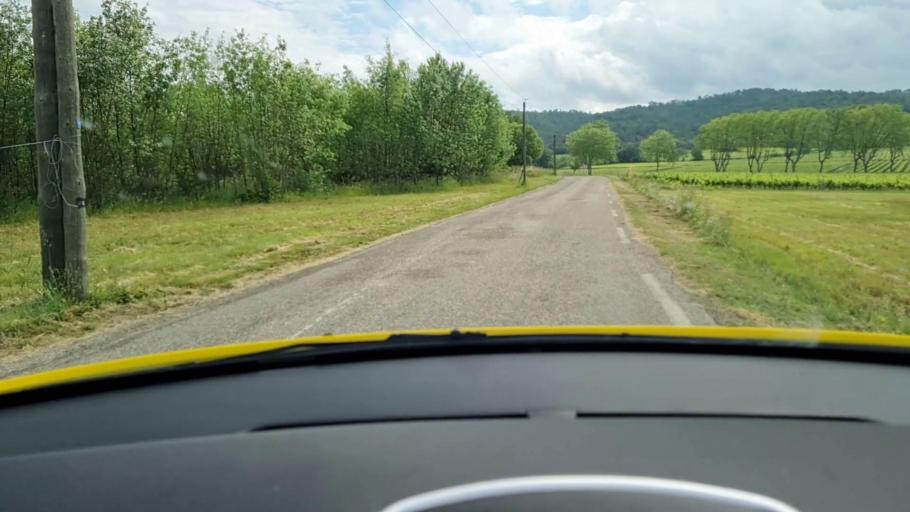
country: FR
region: Languedoc-Roussillon
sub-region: Departement du Gard
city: Quissac
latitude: 43.8560
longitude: 4.0141
